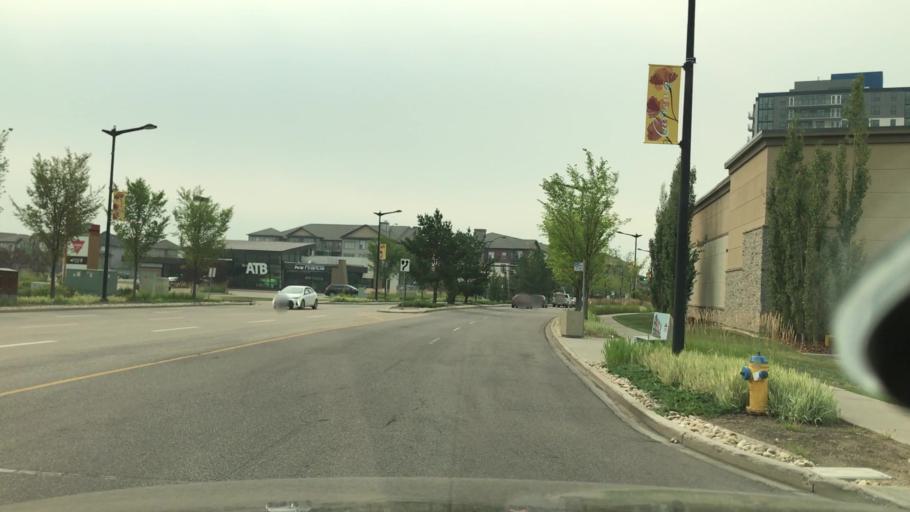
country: CA
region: Alberta
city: Devon
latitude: 53.4359
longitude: -113.5997
